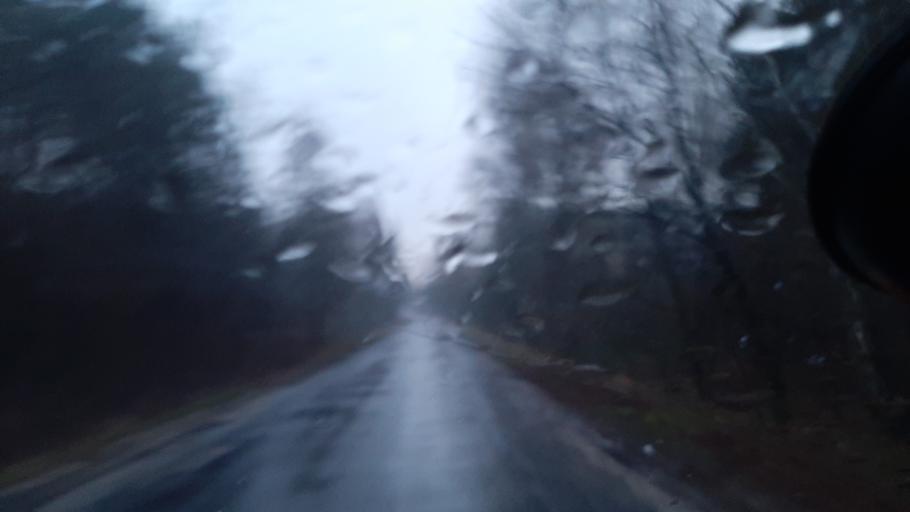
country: PL
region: Lublin Voivodeship
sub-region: Powiat lubartowski
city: Firlej
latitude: 51.5433
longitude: 22.5048
